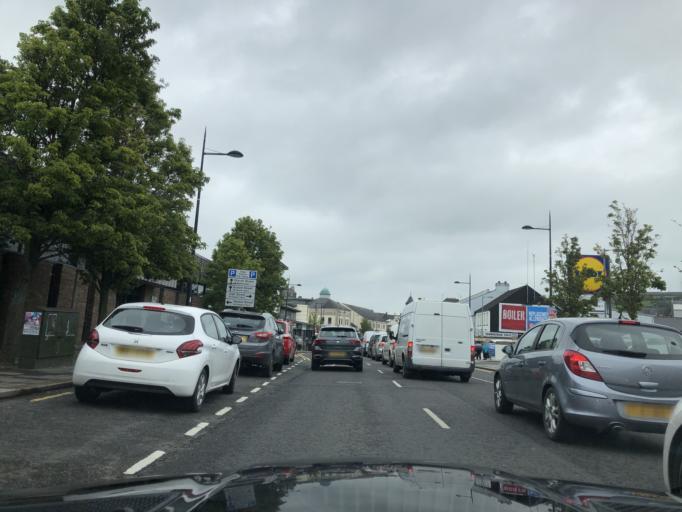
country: GB
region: Northern Ireland
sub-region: Down District
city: Downpatrick
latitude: 54.3260
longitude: -5.7188
